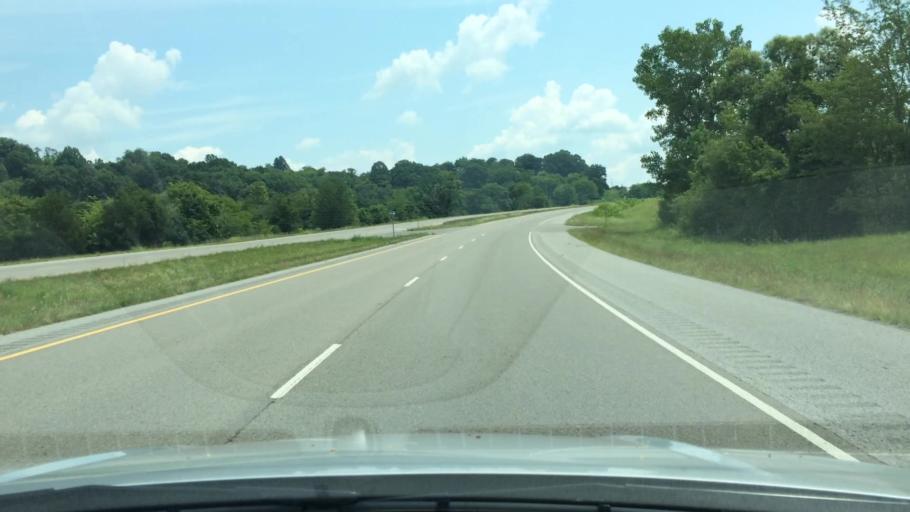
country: US
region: Tennessee
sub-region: Giles County
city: Pulaski
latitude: 35.1750
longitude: -86.9992
